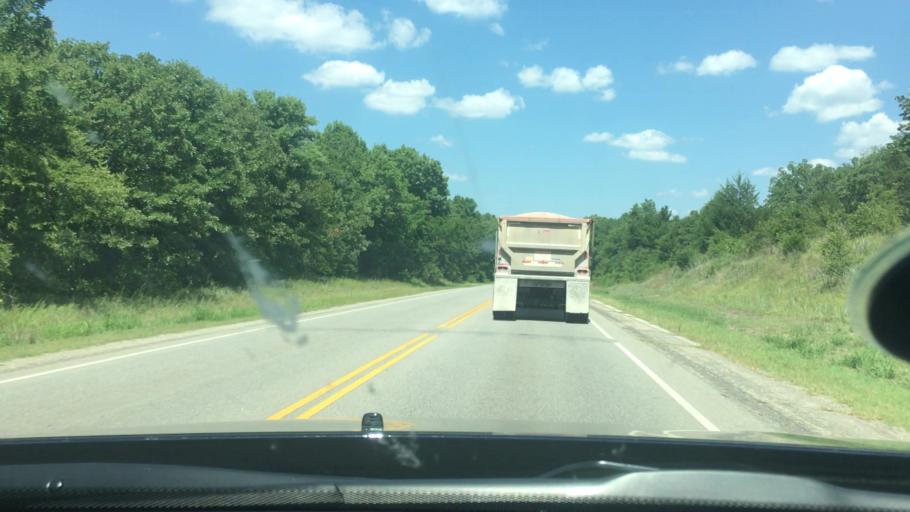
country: US
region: Oklahoma
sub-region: Marshall County
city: Oakland
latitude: 34.1660
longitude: -96.8299
